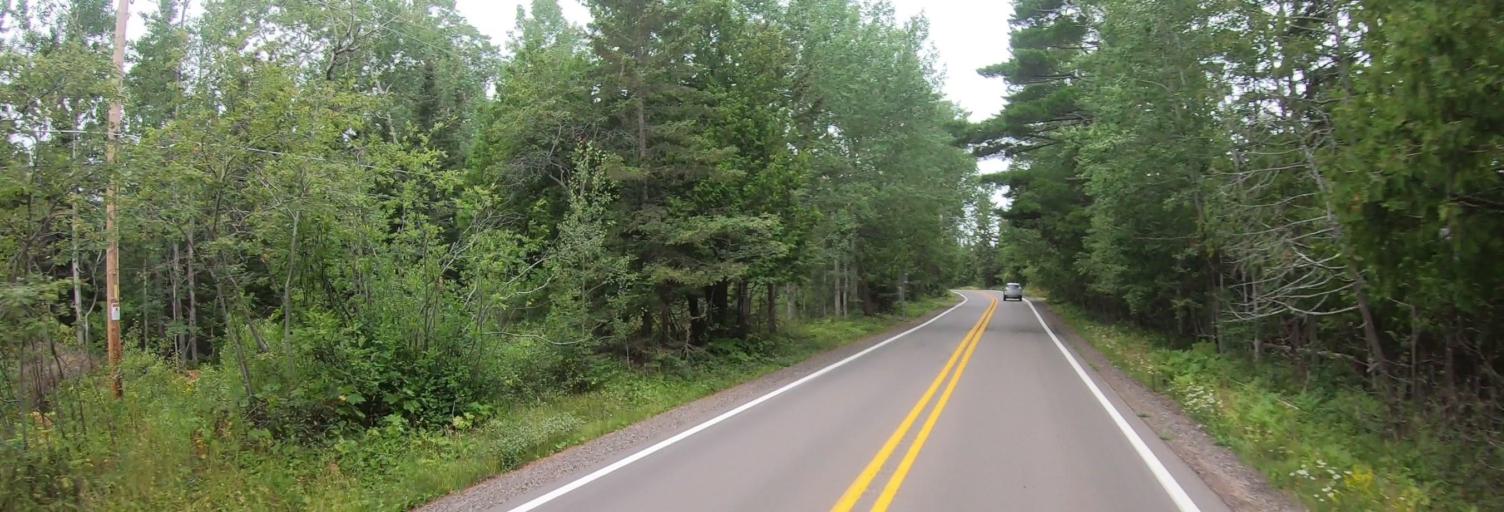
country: US
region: Michigan
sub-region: Keweenaw County
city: Eagle River
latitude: 47.4565
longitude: -88.1442
